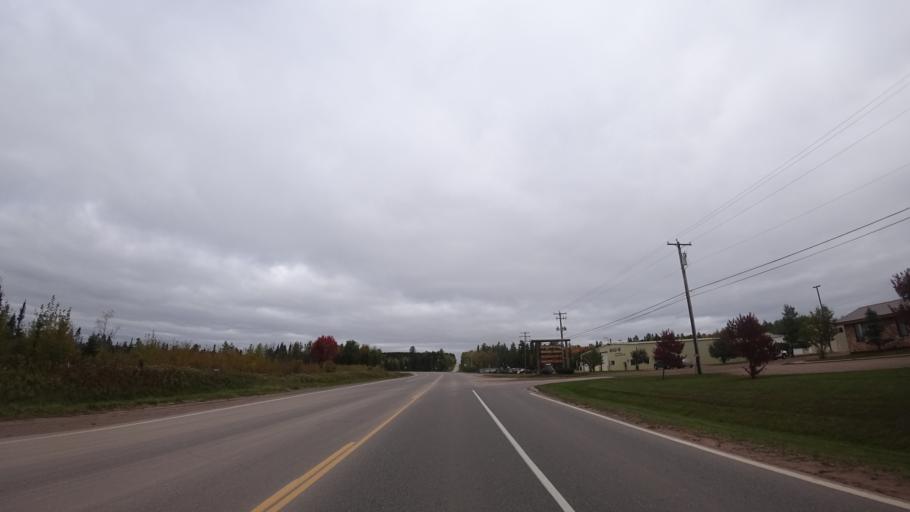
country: US
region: Wisconsin
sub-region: Florence County
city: Florence
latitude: 46.1071
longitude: -88.0758
